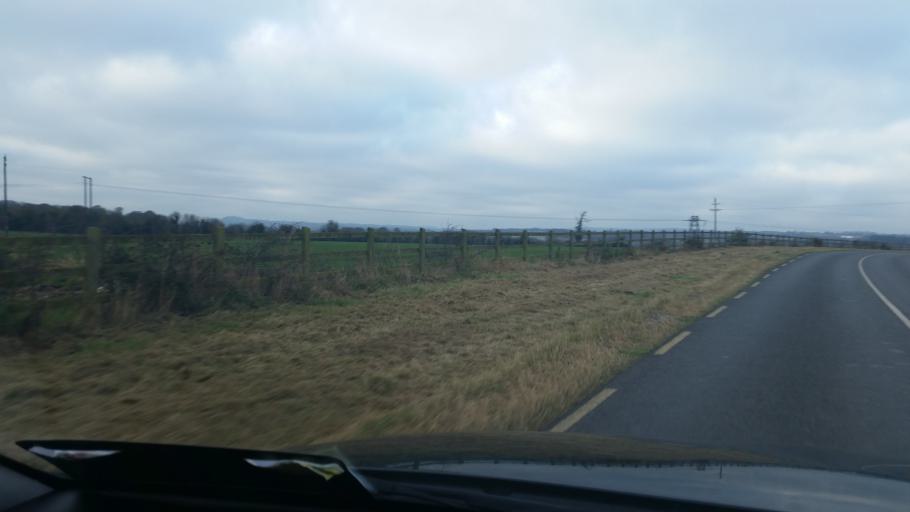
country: IE
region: Leinster
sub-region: Lu
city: Tullyallen
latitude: 53.7104
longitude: -6.4126
